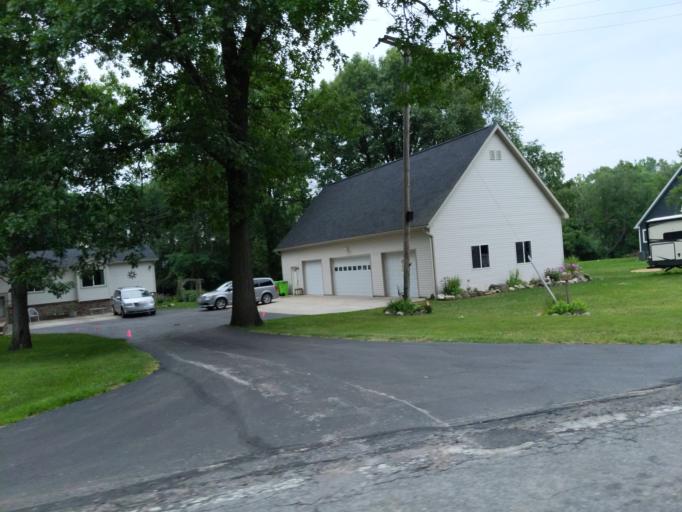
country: US
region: Michigan
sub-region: Livingston County
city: Whitmore Lake
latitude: 42.4425
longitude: -83.7942
